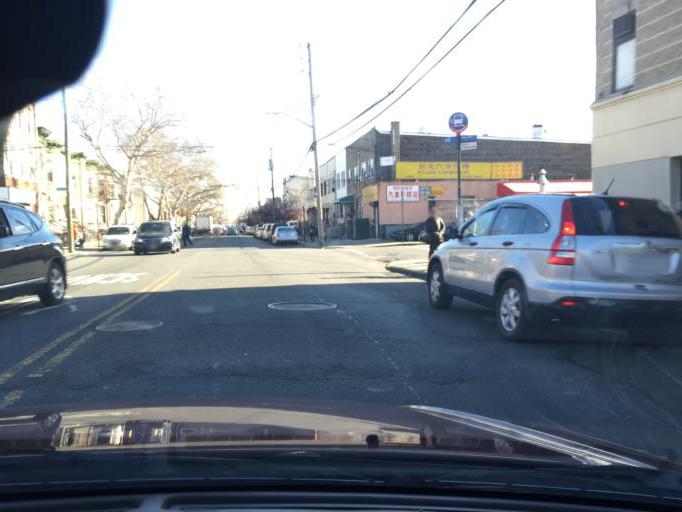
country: US
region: New York
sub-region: Kings County
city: Bensonhurst
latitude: 40.6331
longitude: -74.0055
